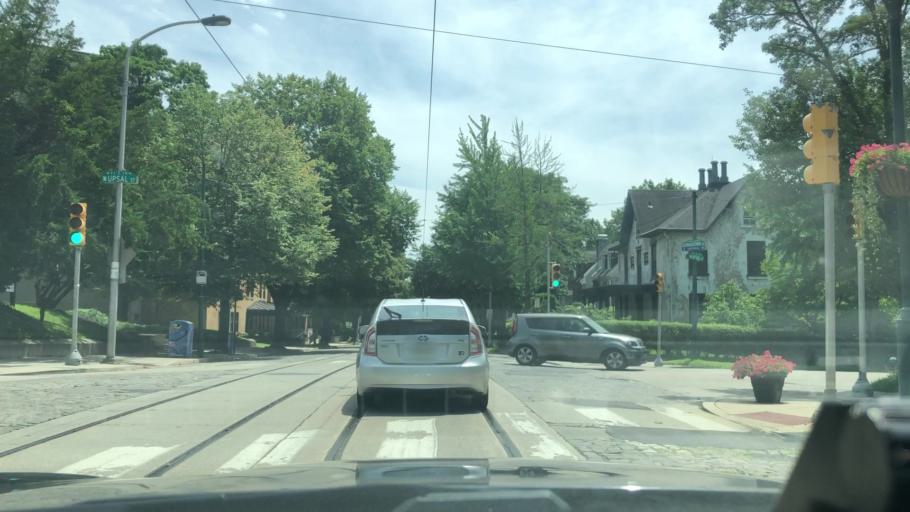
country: US
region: Pennsylvania
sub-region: Montgomery County
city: Wyndmoor
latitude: 40.0486
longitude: -75.1836
